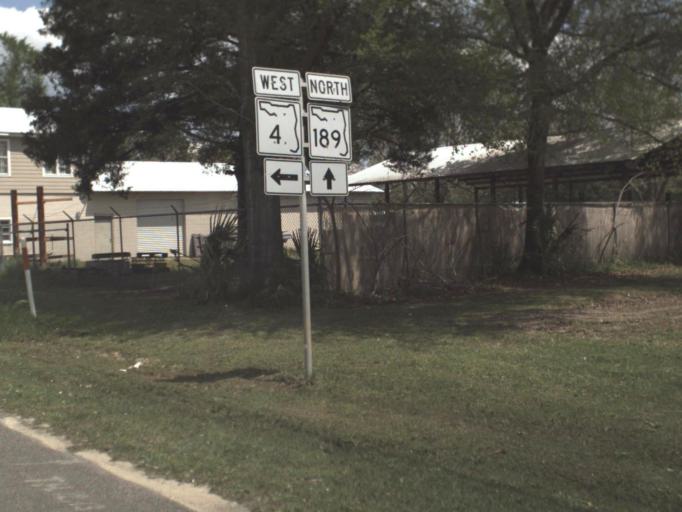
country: US
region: Florida
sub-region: Okaloosa County
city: Crestview
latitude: 30.7961
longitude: -86.6819
